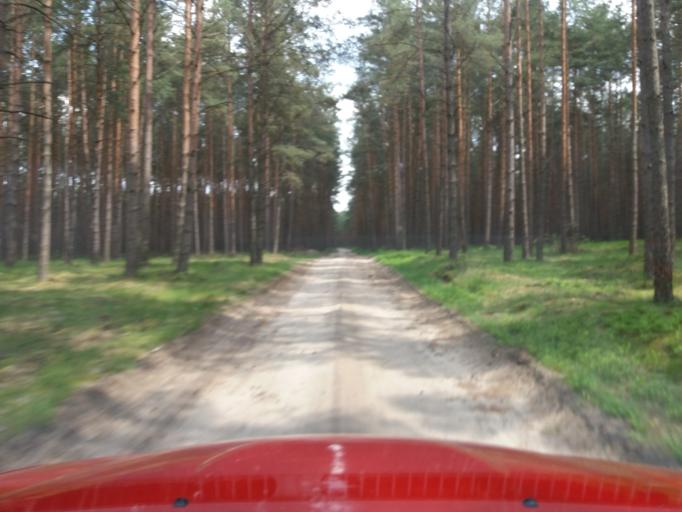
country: PL
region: West Pomeranian Voivodeship
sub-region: Powiat choszczenski
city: Drawno
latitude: 53.1388
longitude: 15.7467
